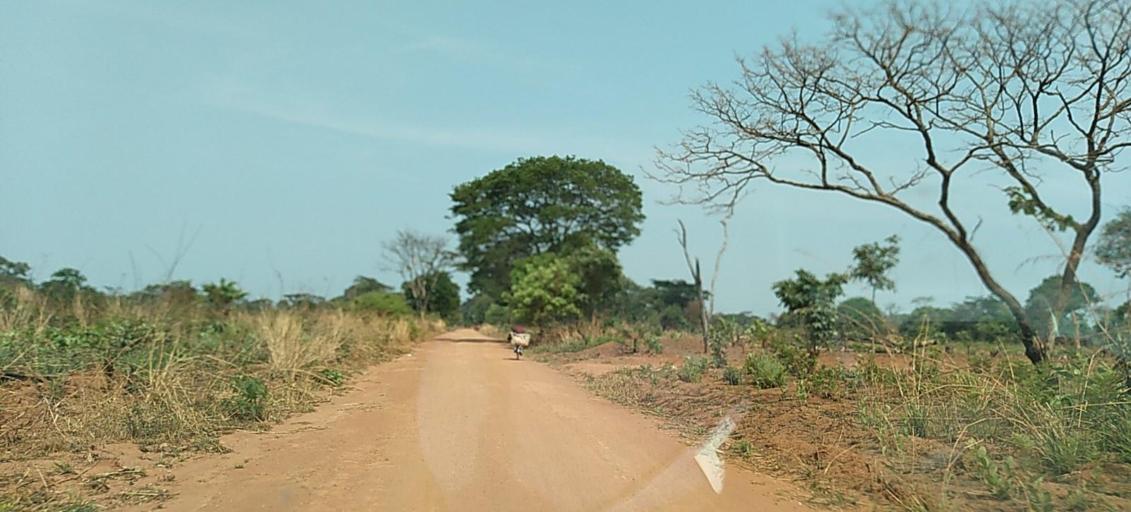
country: ZM
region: Copperbelt
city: Chililabombwe
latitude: -12.3410
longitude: 27.6964
